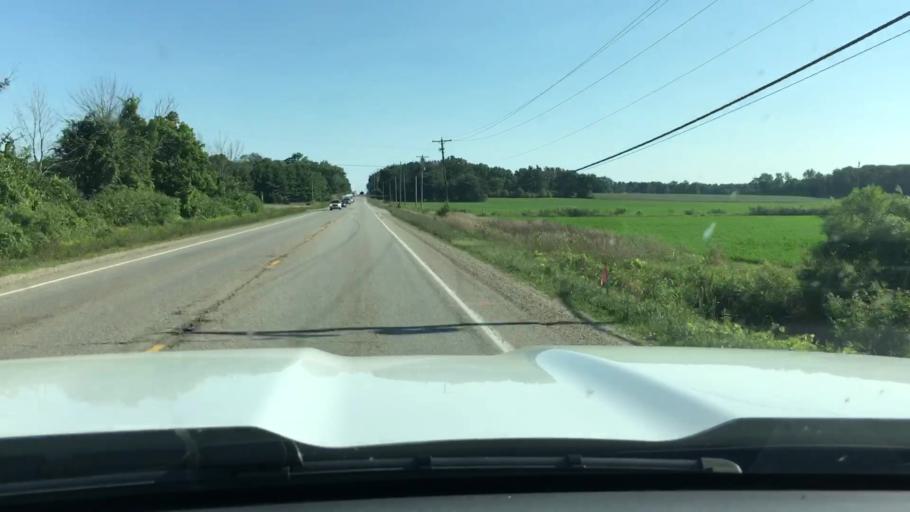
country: US
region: Michigan
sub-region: Ottawa County
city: Allendale
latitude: 43.0029
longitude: -85.9551
